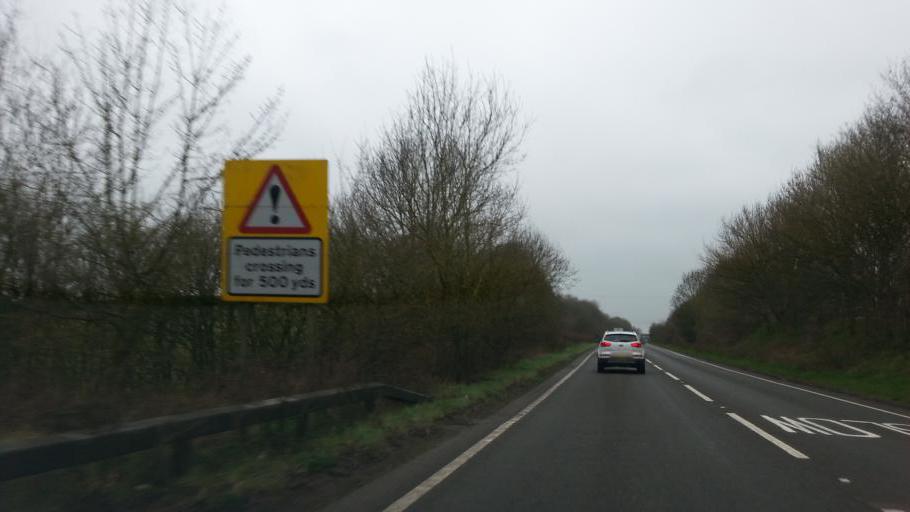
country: GB
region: England
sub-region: Oxfordshire
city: Adderbury
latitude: 52.0684
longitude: -1.2632
